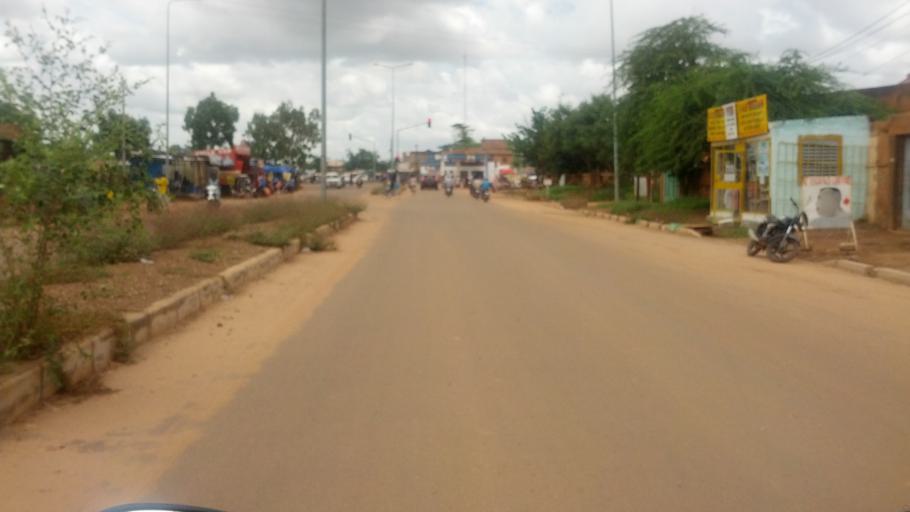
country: BF
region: Centre
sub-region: Kadiogo Province
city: Ouagadougou
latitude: 12.3749
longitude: -1.4970
